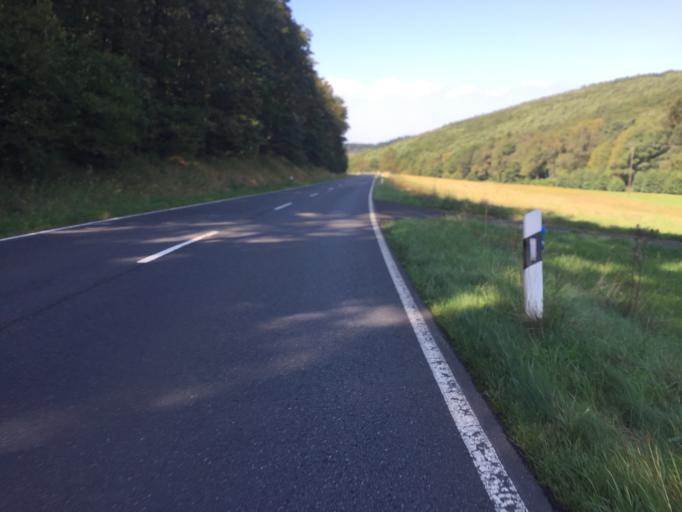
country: DE
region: Hesse
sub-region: Regierungsbezirk Darmstadt
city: Usingen
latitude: 50.4161
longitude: 8.5741
